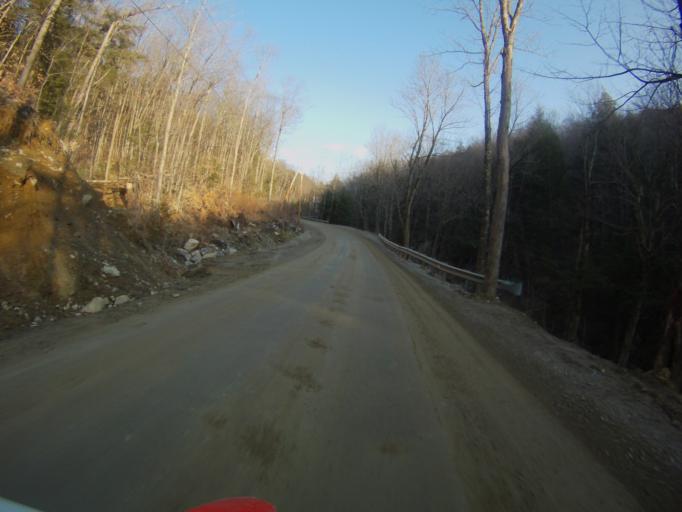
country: US
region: Vermont
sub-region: Addison County
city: Bristol
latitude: 44.0780
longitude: -73.0644
